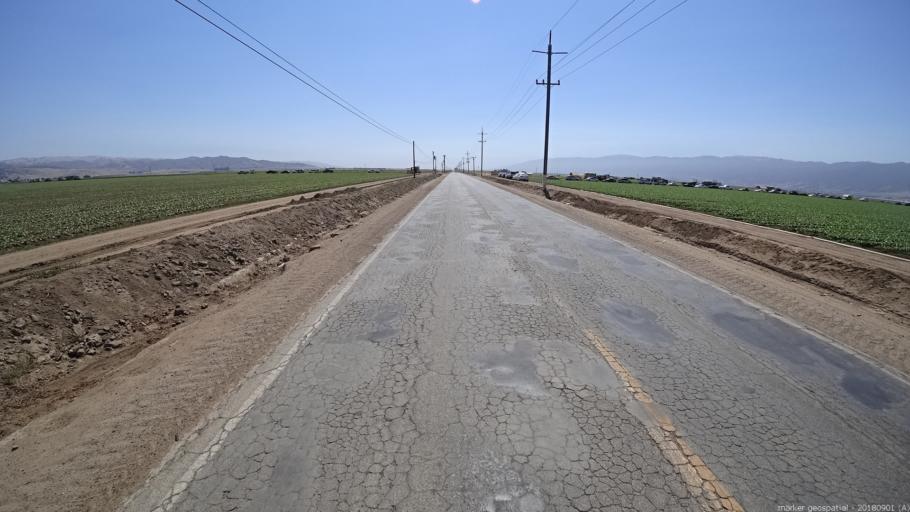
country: US
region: California
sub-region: Monterey County
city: Chualar
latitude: 36.6150
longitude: -121.5214
